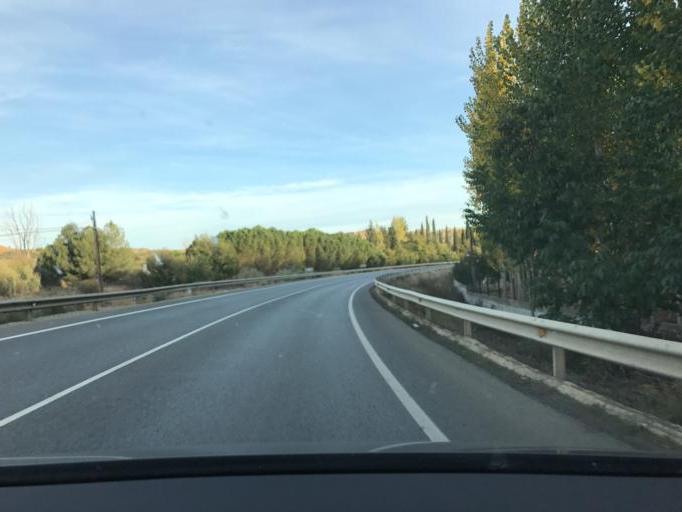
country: ES
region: Andalusia
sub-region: Provincia de Granada
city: Guadix
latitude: 37.2849
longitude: -3.1175
